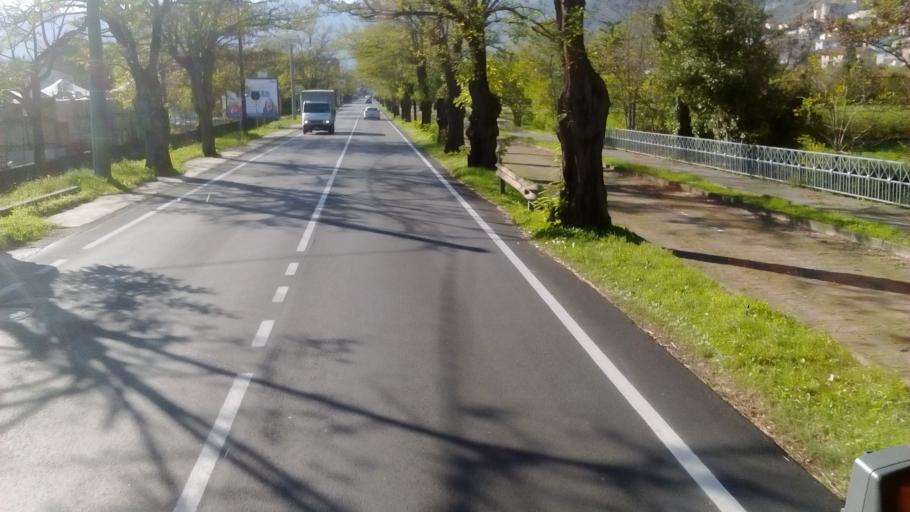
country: IT
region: Molise
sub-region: Provincia di Isernia
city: Venafro
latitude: 41.4880
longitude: 14.0559
